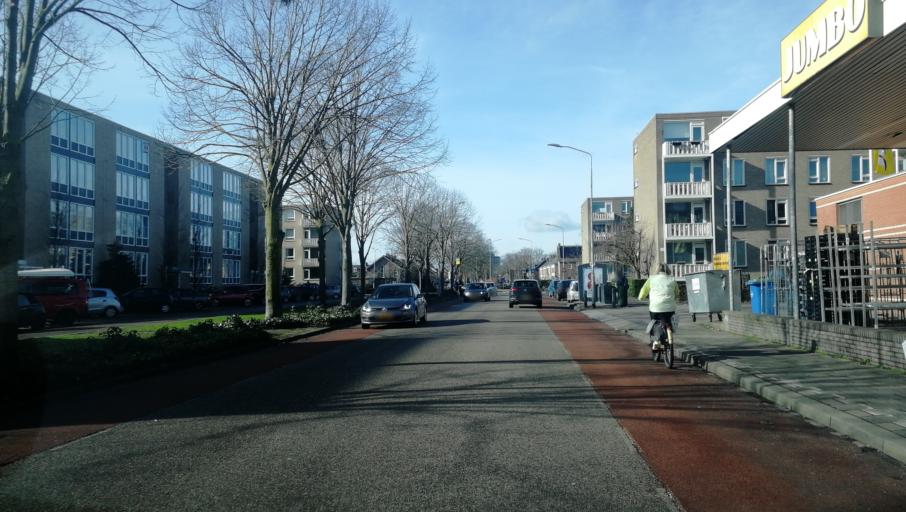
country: NL
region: Limburg
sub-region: Gemeente Venlo
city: Venlo
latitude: 51.3695
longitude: 6.1872
